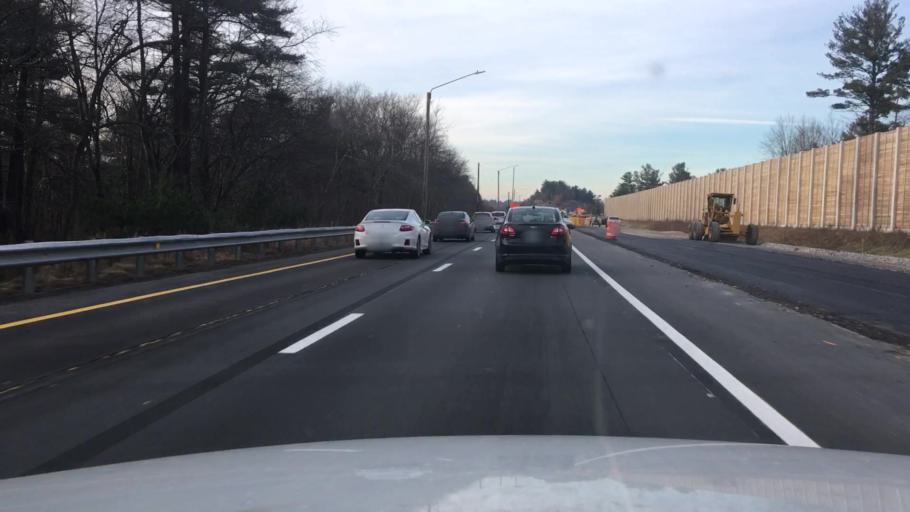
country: US
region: New Hampshire
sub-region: Hillsborough County
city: Manchester
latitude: 42.9507
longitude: -71.3983
